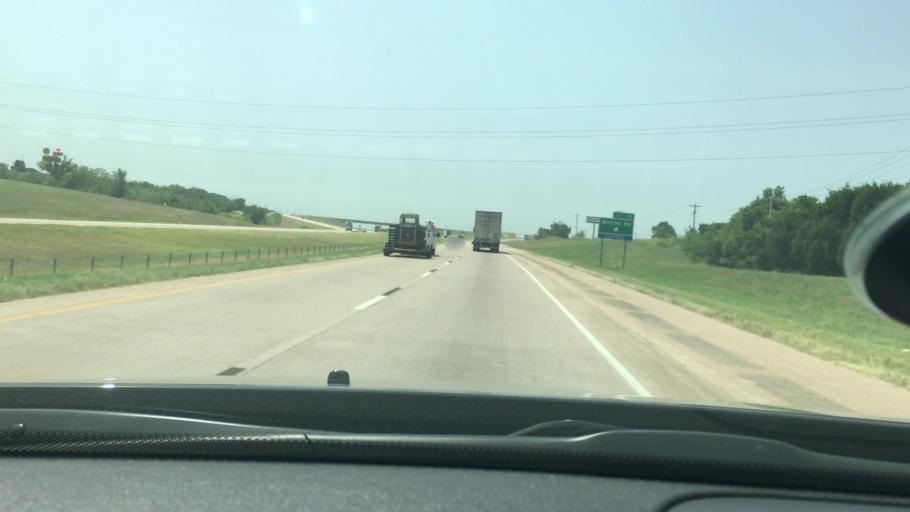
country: US
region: Oklahoma
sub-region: Garvin County
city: Pauls Valley
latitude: 34.7122
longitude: -97.2492
